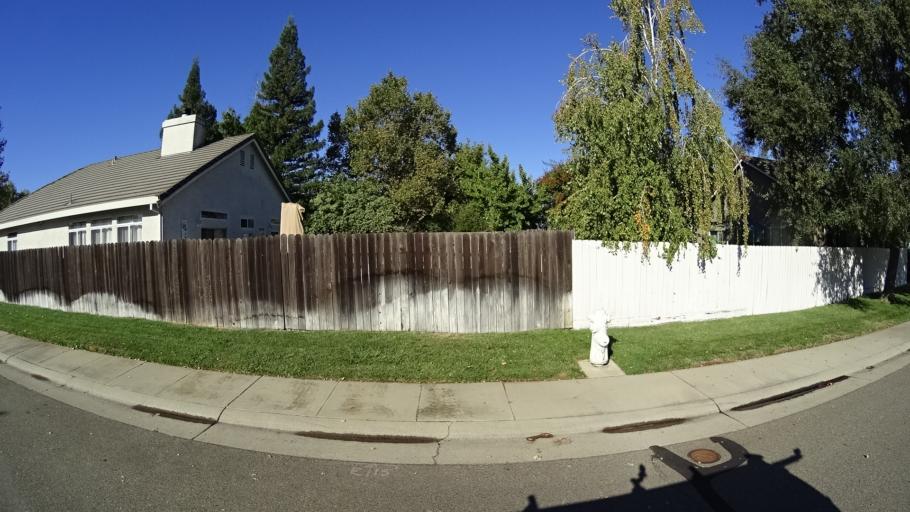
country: US
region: California
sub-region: Sacramento County
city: Elk Grove
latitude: 38.4390
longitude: -121.3871
